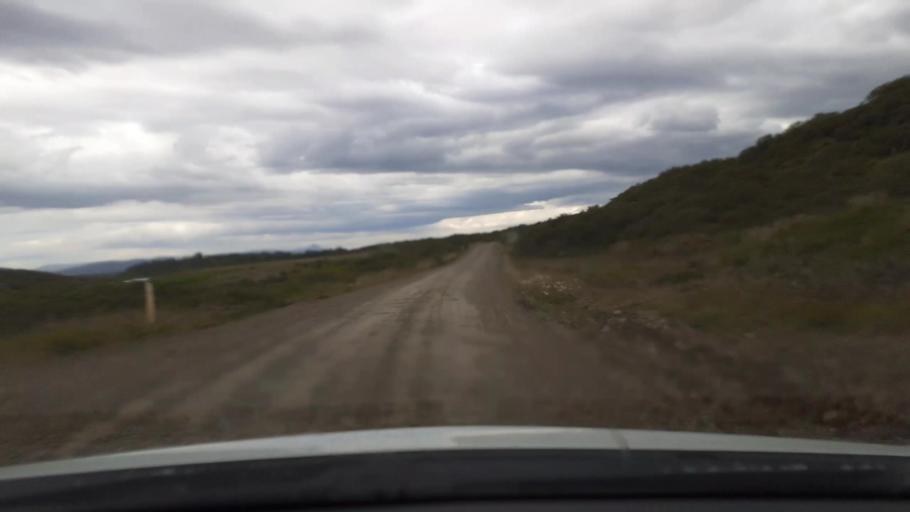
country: IS
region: West
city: Borgarnes
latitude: 64.6076
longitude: -21.9630
